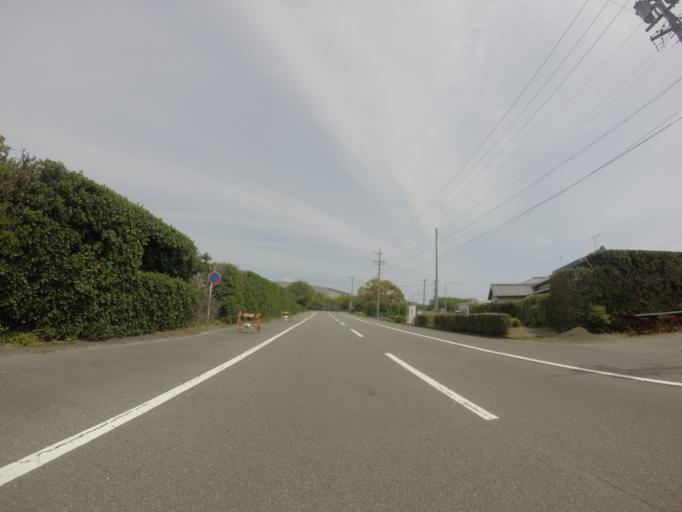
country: JP
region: Shizuoka
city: Fujieda
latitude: 34.7823
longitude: 138.2959
